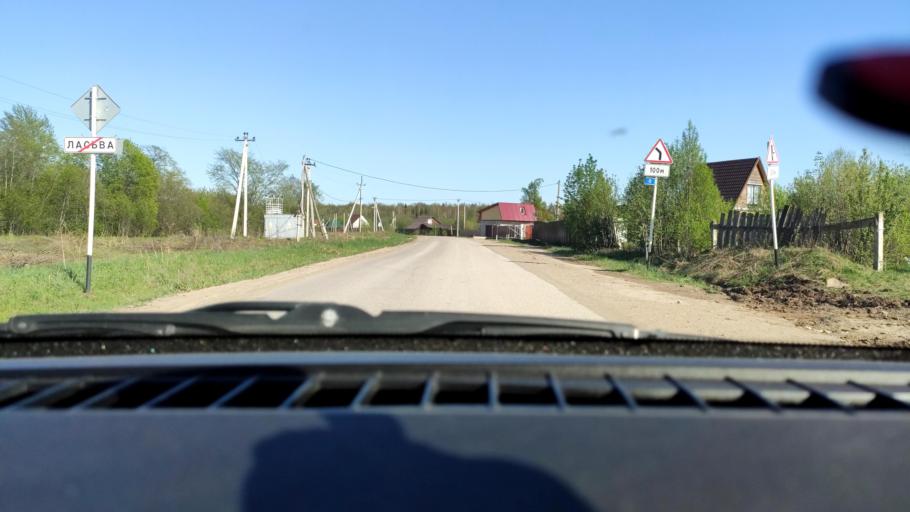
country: RU
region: Perm
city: Overyata
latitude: 58.0782
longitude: 55.9774
